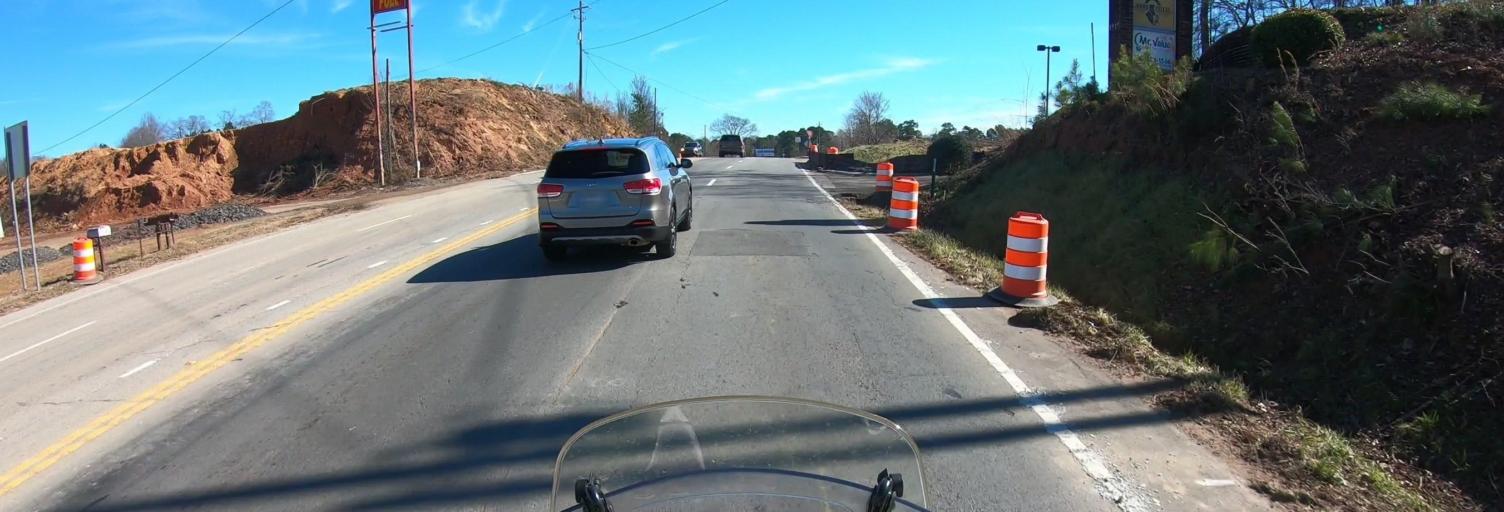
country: US
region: Georgia
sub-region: Forsyth County
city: Cumming
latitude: 34.2629
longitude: -84.0854
